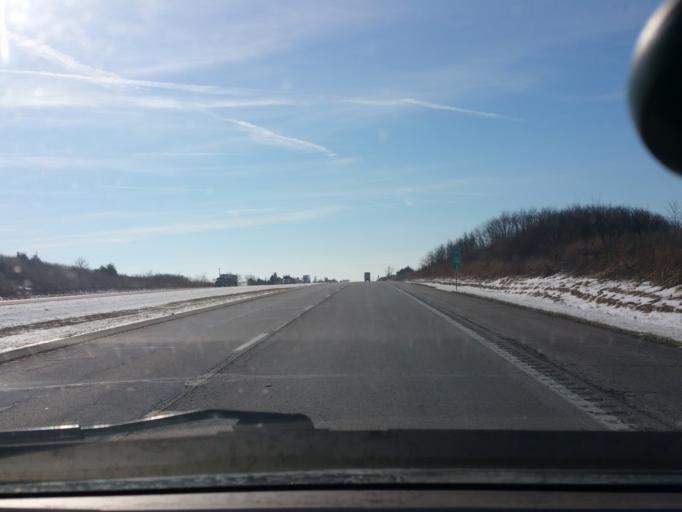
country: US
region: Iowa
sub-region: Decatur County
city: Lamoni
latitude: 40.4996
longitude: -93.9678
